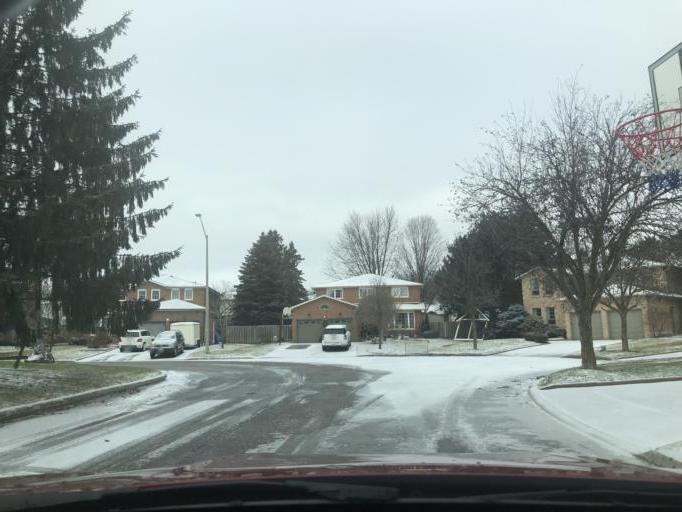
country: CA
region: Ontario
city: Markham
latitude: 43.8746
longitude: -79.2364
